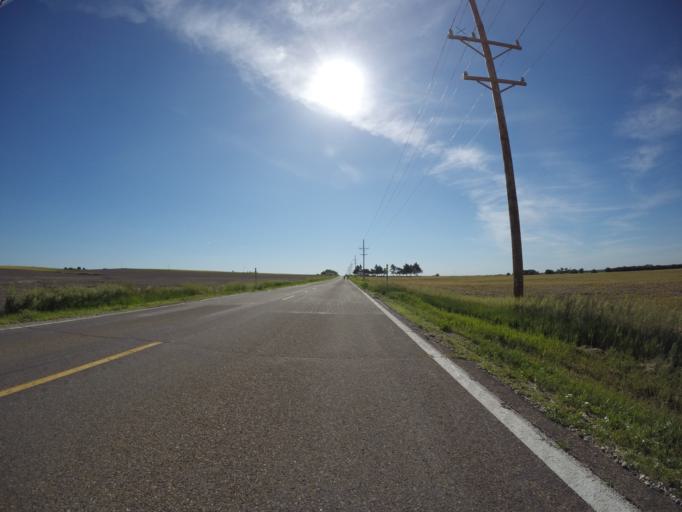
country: US
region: Kansas
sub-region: Mitchell County
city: Beloit
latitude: 39.6393
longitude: -97.9356
